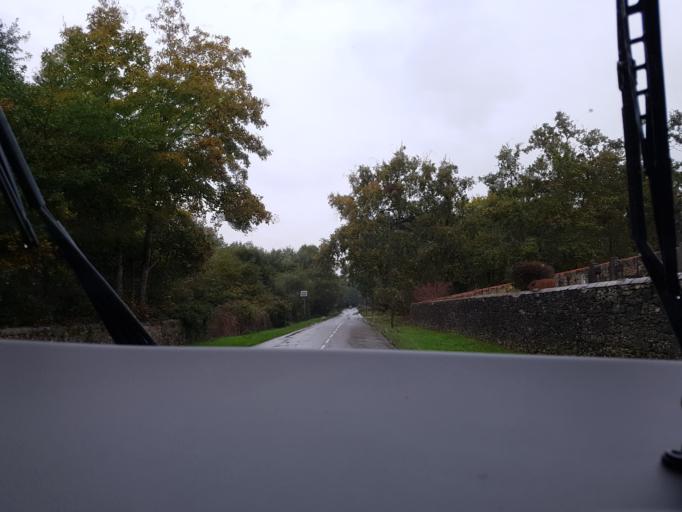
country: FR
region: Aquitaine
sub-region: Departement de la Gironde
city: Saint-Symphorien
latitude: 44.3264
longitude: -0.5848
